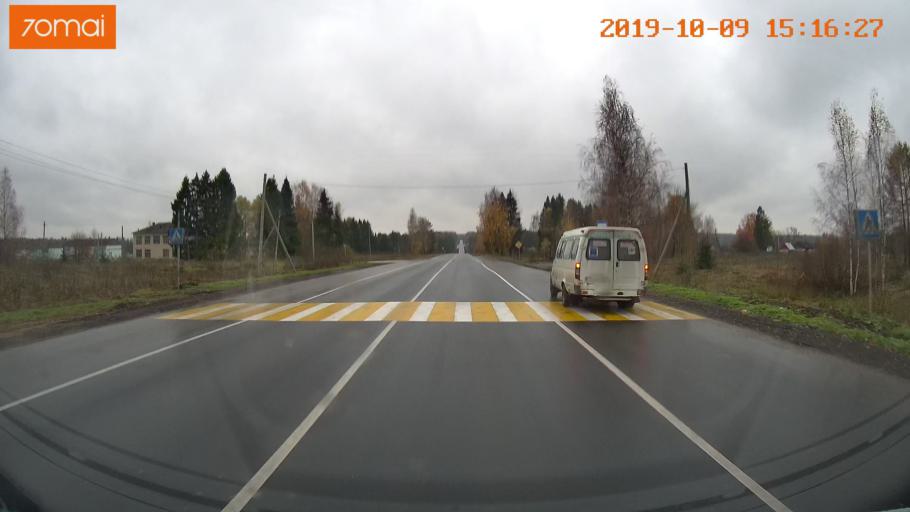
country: RU
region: Kostroma
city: Susanino
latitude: 58.1102
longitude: 41.5859
